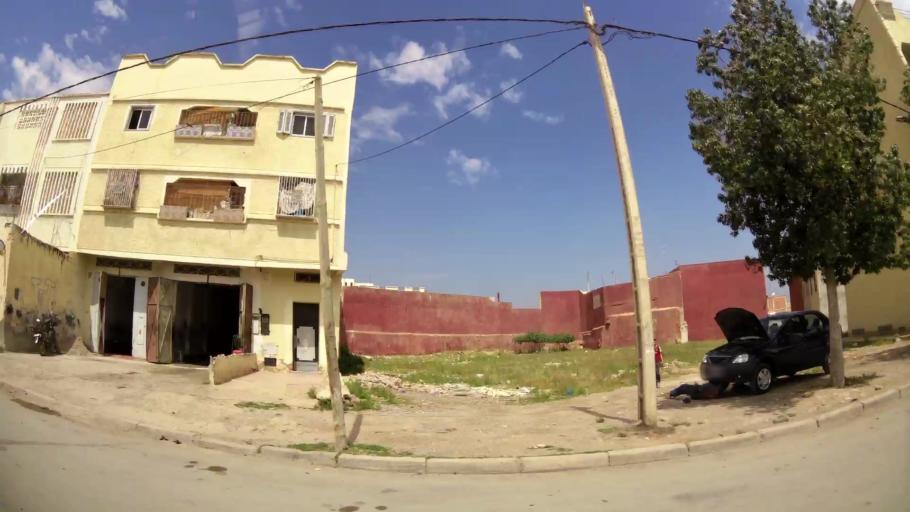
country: MA
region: Oriental
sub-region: Oujda-Angad
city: Oujda
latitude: 34.6854
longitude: -1.9028
